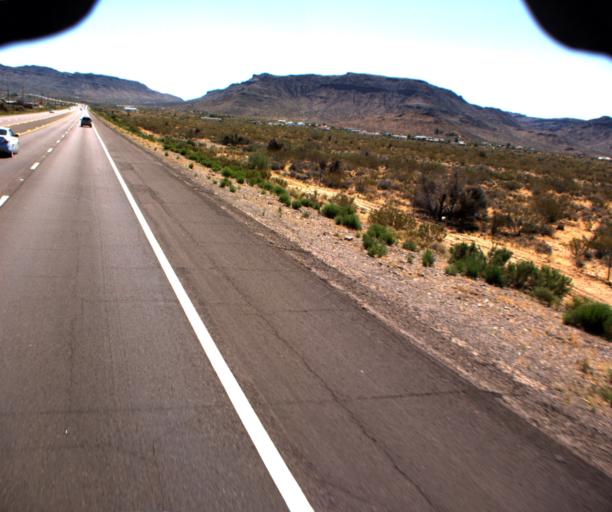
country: US
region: Arizona
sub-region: Mohave County
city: Golden Valley
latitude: 35.2193
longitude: -114.1621
